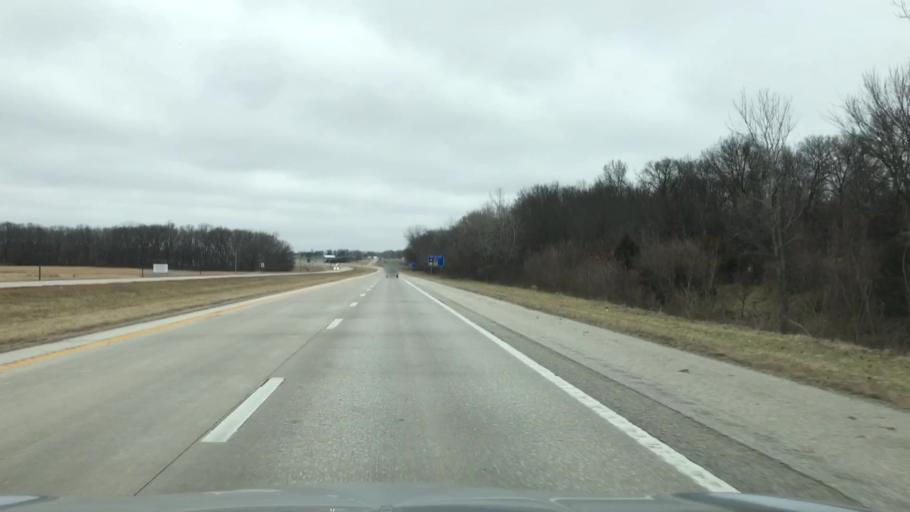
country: US
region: Missouri
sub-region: Linn County
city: Brookfield
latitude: 39.7751
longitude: -93.0881
